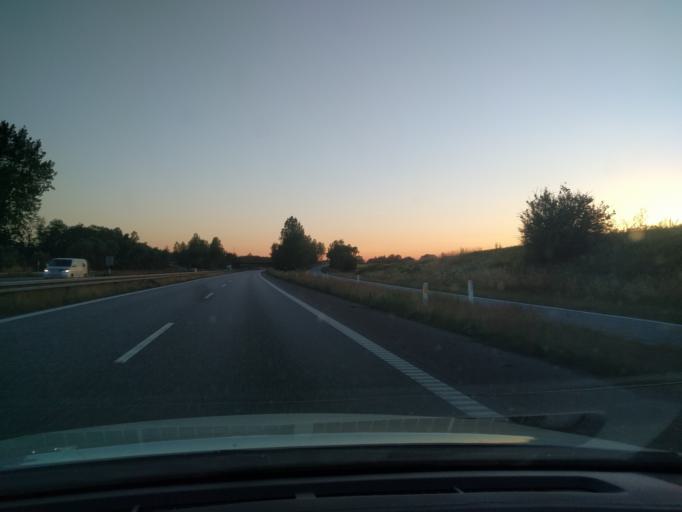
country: DK
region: South Denmark
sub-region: Nyborg Kommune
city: Nyborg
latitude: 55.3321
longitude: 10.7478
